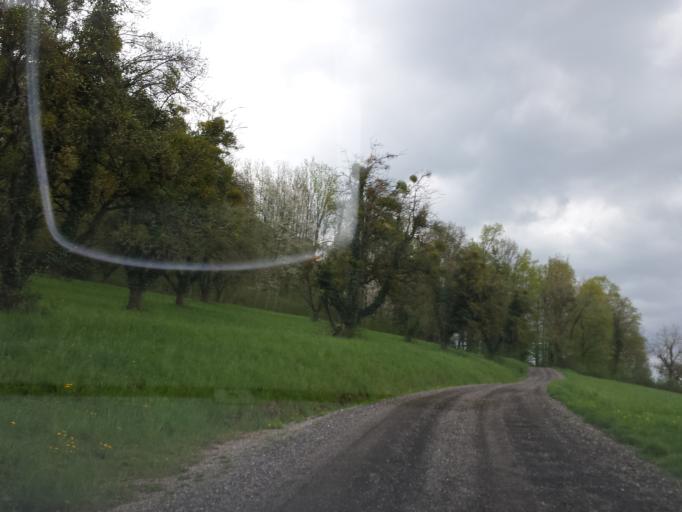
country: AT
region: Styria
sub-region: Politischer Bezirk Suedoststeiermark
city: Riegersburg
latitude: 47.0052
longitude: 15.9291
